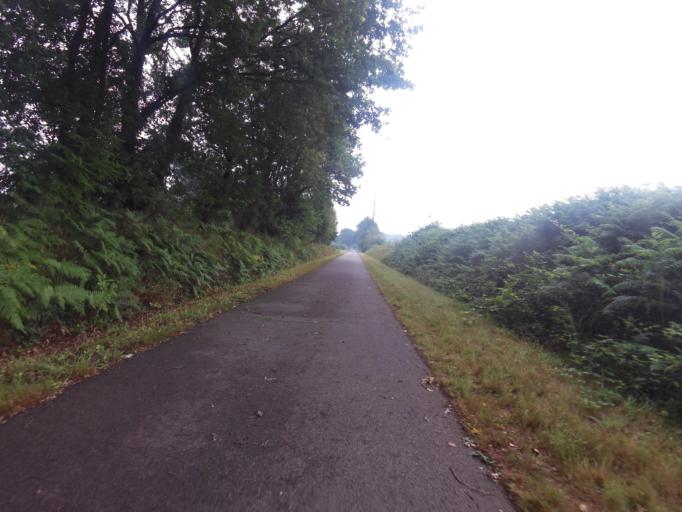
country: FR
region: Brittany
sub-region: Departement du Morbihan
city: Guillac
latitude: 47.9010
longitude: -2.4347
